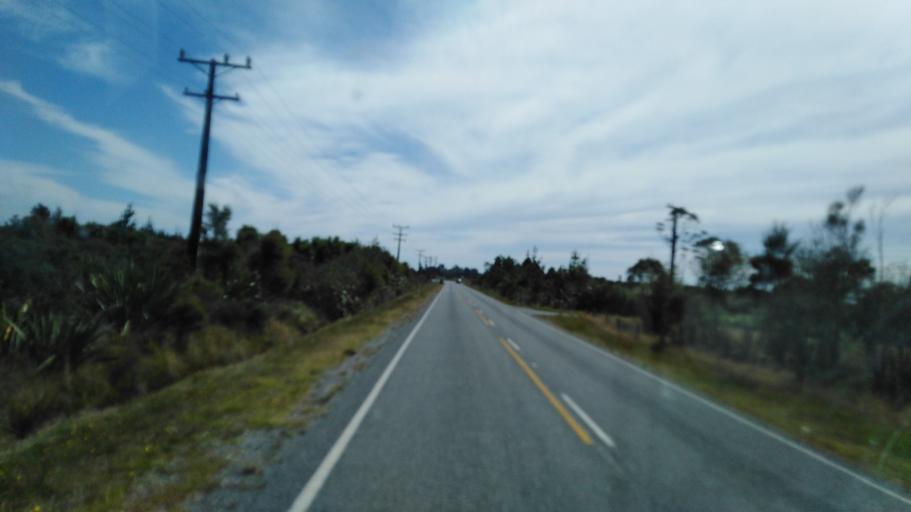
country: NZ
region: West Coast
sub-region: Buller District
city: Westport
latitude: -41.7383
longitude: 171.7067
